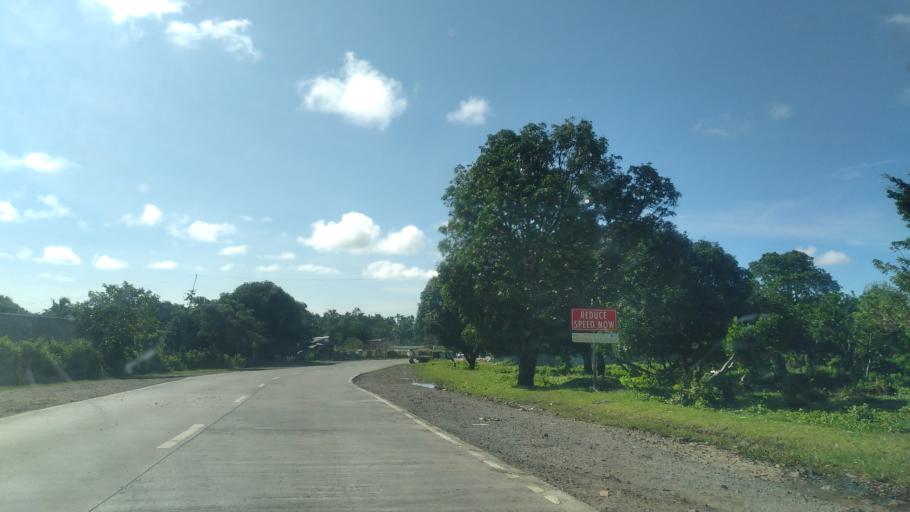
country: PH
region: Calabarzon
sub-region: Province of Quezon
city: Isabang
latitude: 13.9552
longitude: 121.5789
